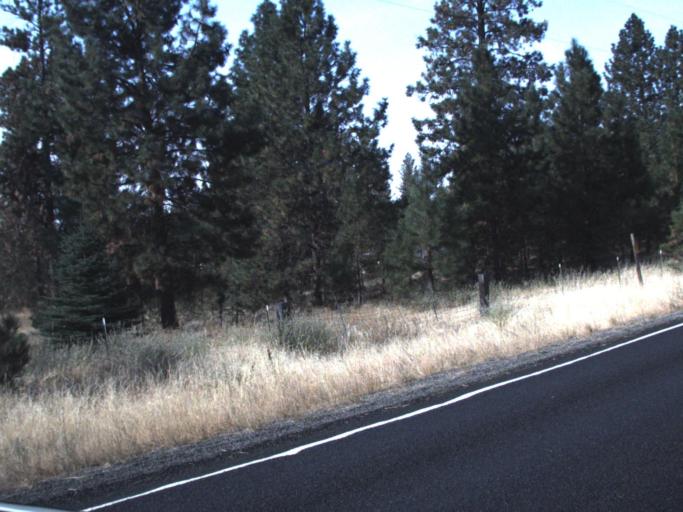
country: US
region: Washington
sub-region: Spokane County
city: Fairchild Air Force Base
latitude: 47.8392
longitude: -117.7821
